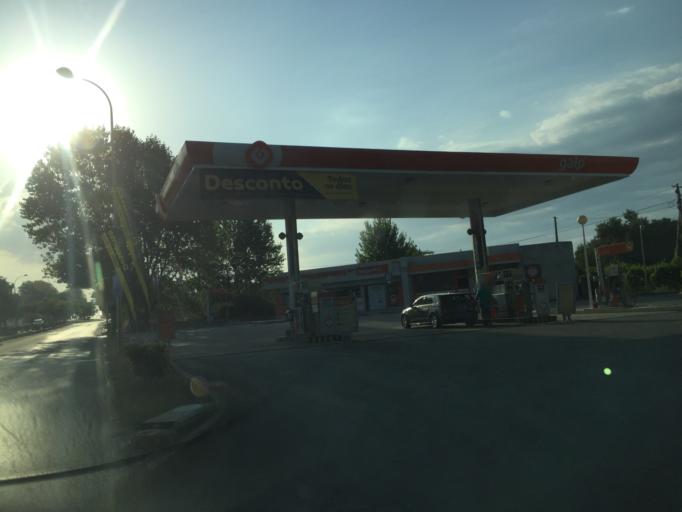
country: PT
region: Santarem
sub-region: Torres Novas
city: Torres Novas
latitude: 39.4732
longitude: -8.5508
